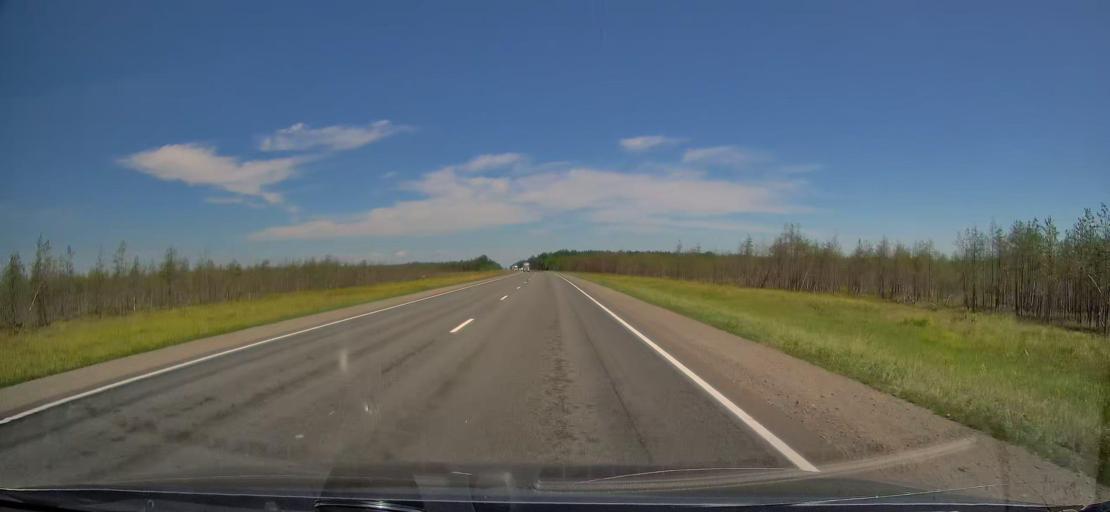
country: RU
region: Vologda
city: Khokhlovo
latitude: 58.9404
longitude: 37.2797
